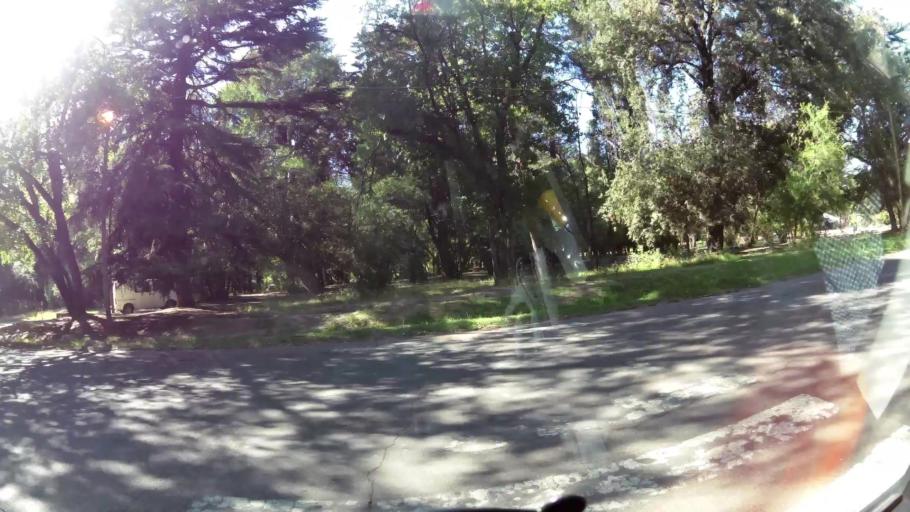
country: AR
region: Mendoza
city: Mendoza
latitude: -32.8868
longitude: -68.8703
